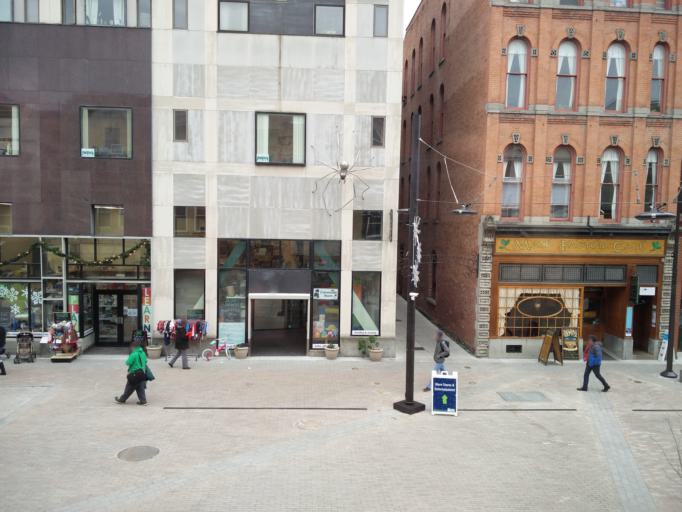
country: US
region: New York
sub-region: Tompkins County
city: Ithaca
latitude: 42.4395
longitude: -76.4973
